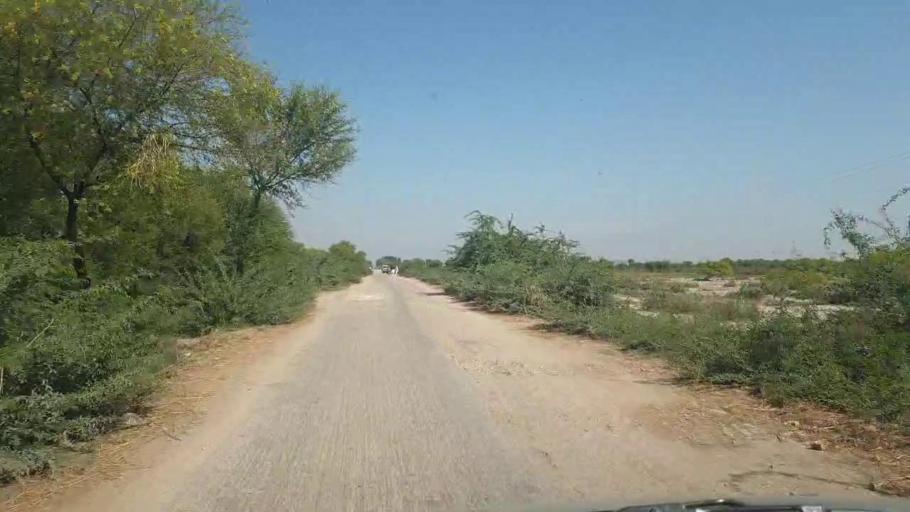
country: PK
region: Sindh
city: Tando Bago
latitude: 24.8153
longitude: 68.9832
